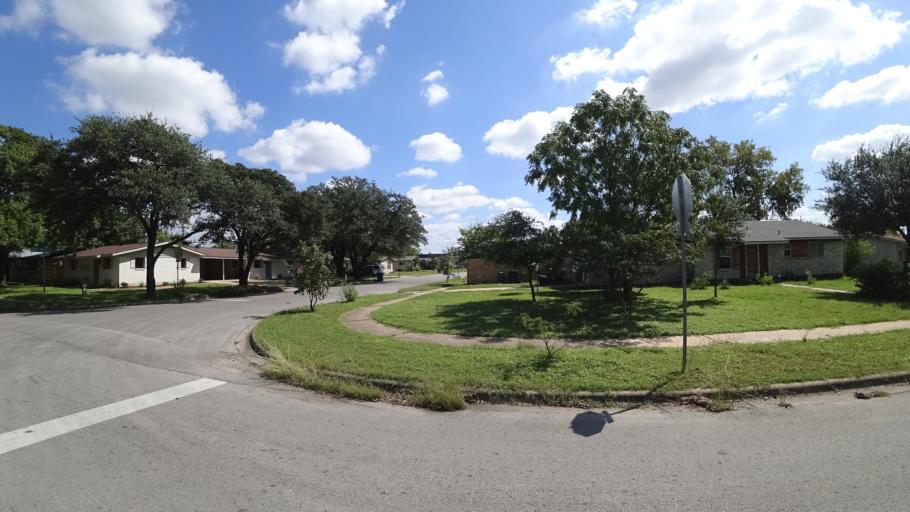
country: US
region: Texas
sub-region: Travis County
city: Austin
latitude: 30.3370
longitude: -97.7088
